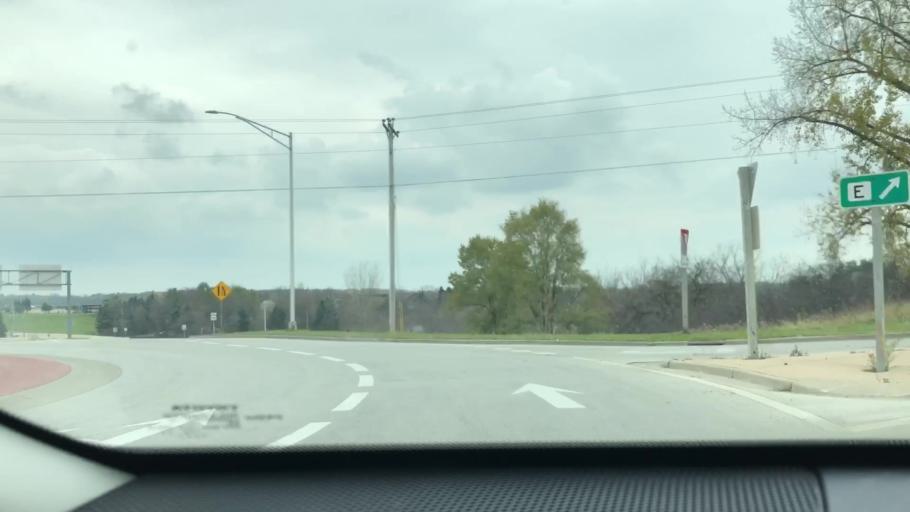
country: US
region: Wisconsin
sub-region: Brown County
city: Oneida
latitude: 44.5000
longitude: -88.1767
